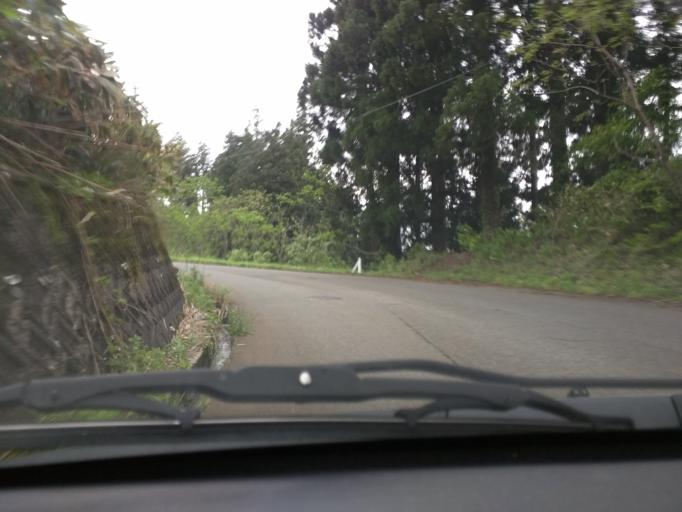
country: JP
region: Niigata
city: Muikamachi
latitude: 37.2226
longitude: 138.9521
